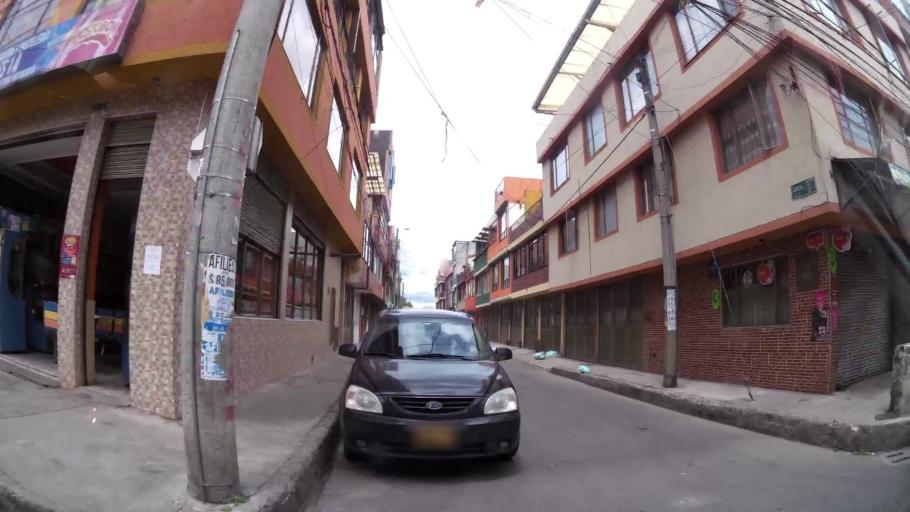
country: CO
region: Cundinamarca
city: Funza
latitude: 4.7098
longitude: -74.1303
